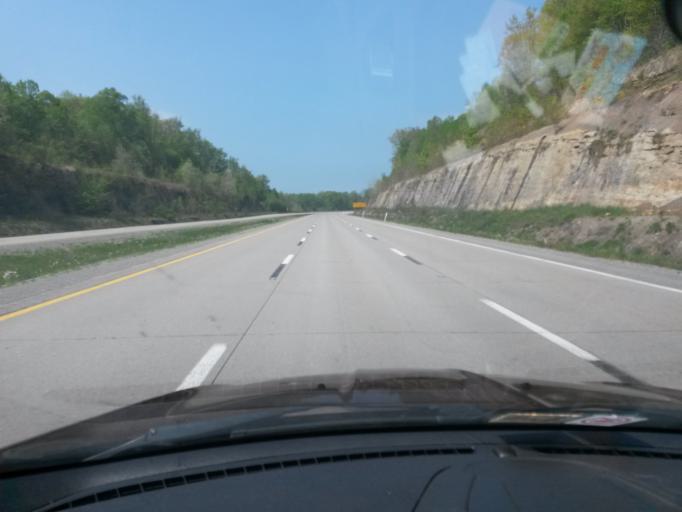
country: US
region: West Virginia
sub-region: Barbour County
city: Belington
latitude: 38.9630
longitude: -80.0246
